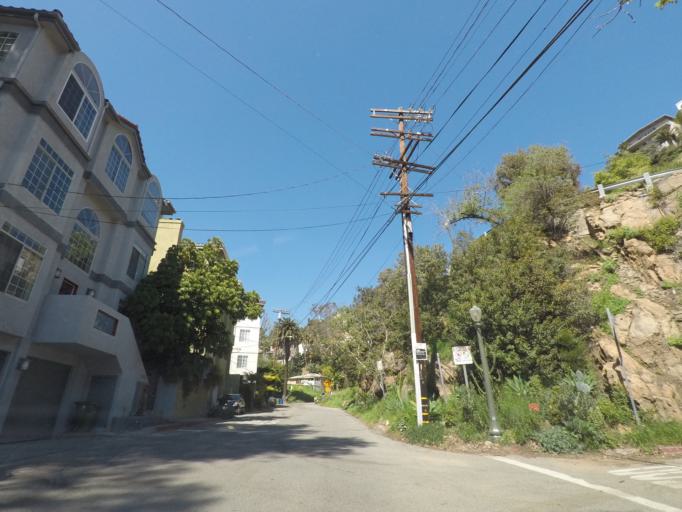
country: US
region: California
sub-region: Los Angeles County
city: Hollywood
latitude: 34.1134
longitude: -118.3307
